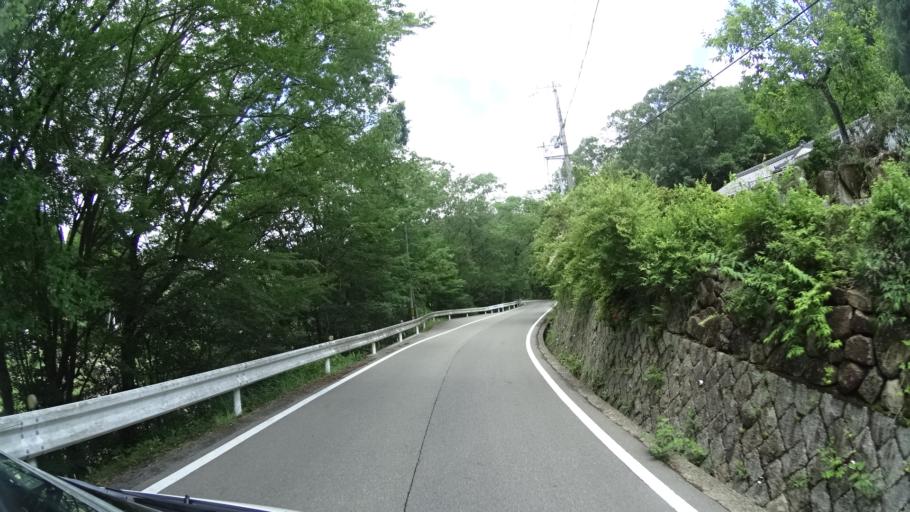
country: JP
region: Hyogo
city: Sasayama
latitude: 35.0227
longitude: 135.3929
